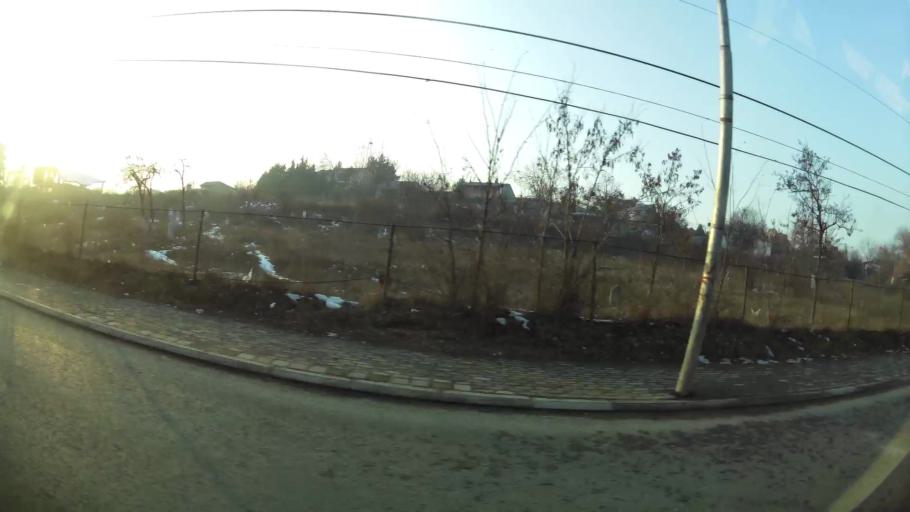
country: MK
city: Creshevo
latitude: 42.0123
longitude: 21.5097
